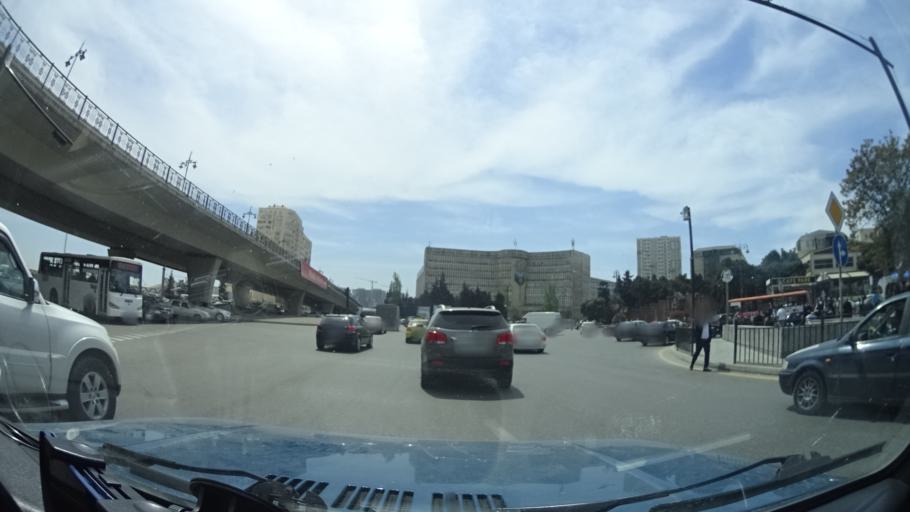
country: AZ
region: Baki
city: Khodzhi-Gasan
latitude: 40.4045
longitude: 49.8072
